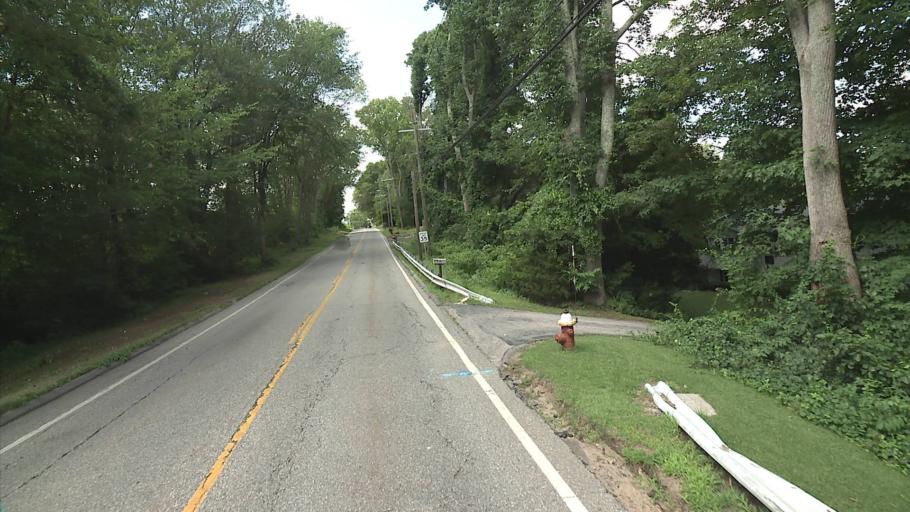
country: US
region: Connecticut
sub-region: New London County
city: Niantic
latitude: 41.3789
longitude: -72.2152
